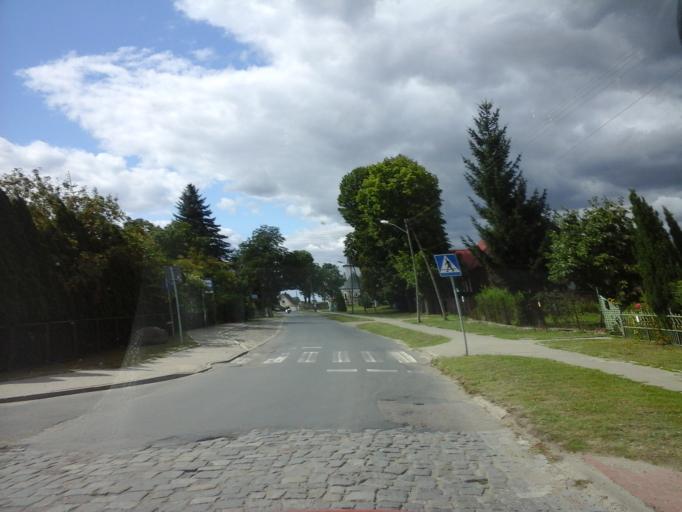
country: PL
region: West Pomeranian Voivodeship
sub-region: Powiat policki
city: Przeclaw
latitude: 53.4136
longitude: 14.4324
